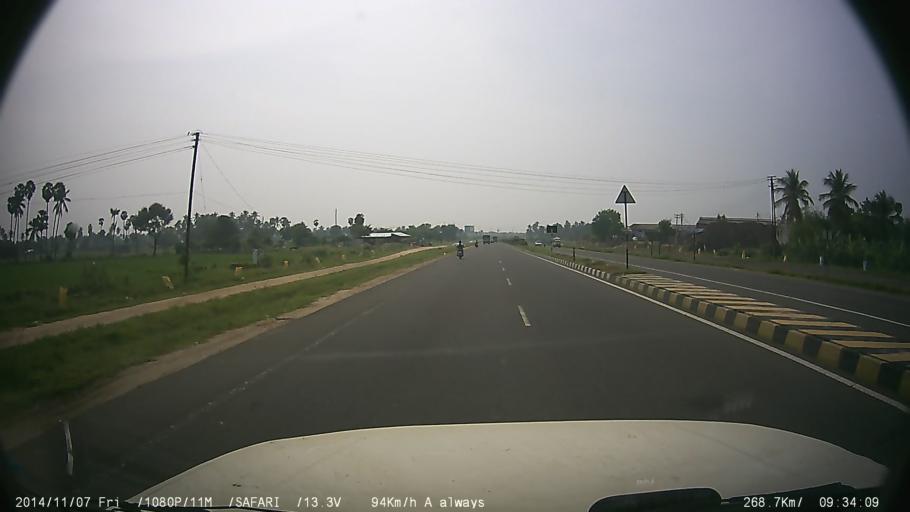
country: IN
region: Tamil Nadu
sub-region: Erode
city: Bhavani
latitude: 11.3907
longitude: 77.6523
